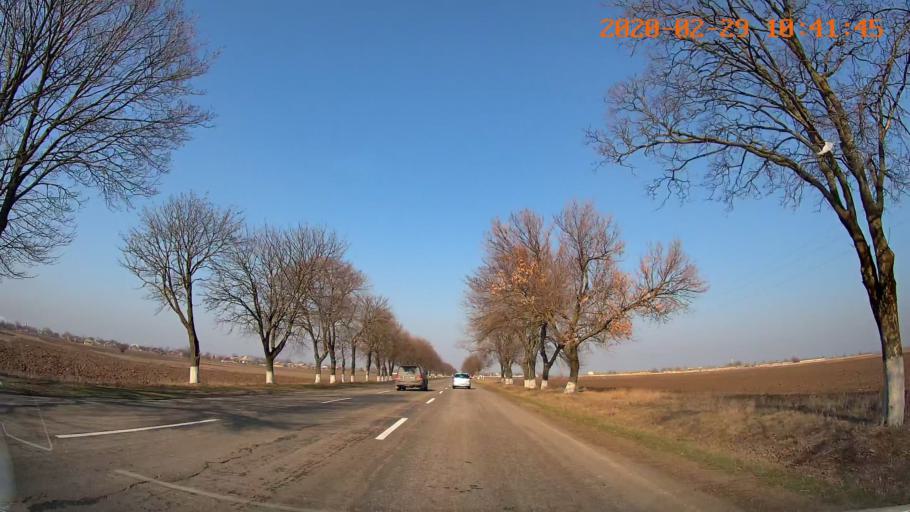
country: MD
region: Telenesti
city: Grigoriopol
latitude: 47.0453
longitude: 29.4207
